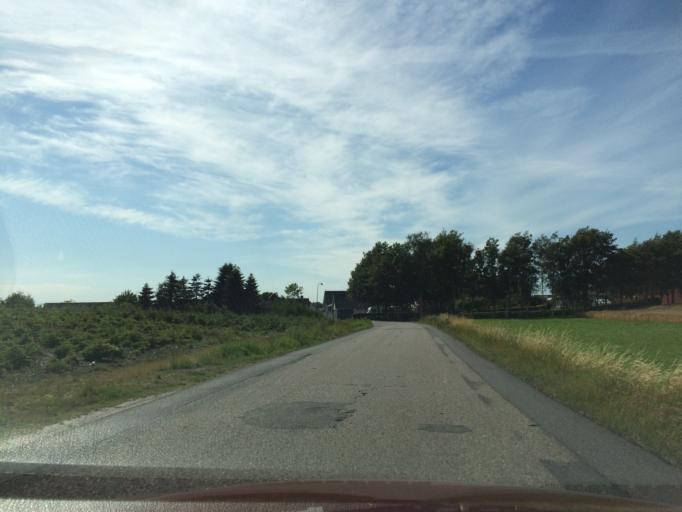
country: DK
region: Central Jutland
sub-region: Silkeborg Kommune
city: Silkeborg
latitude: 56.2237
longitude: 9.5670
